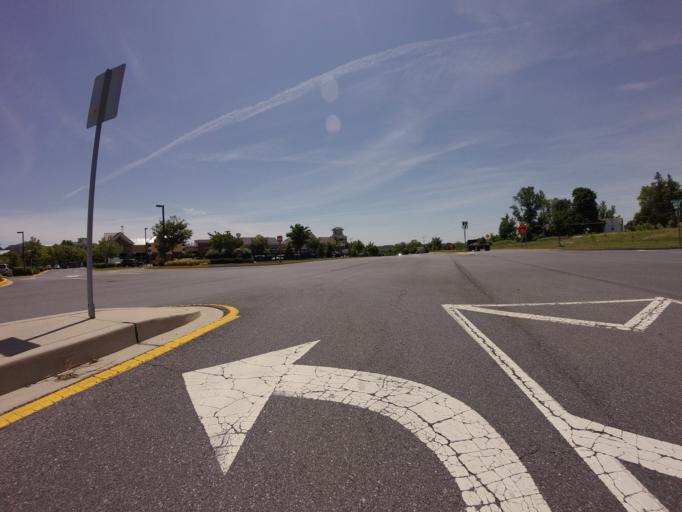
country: US
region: Maryland
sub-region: Frederick County
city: Urbana
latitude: 39.3263
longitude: -77.3437
